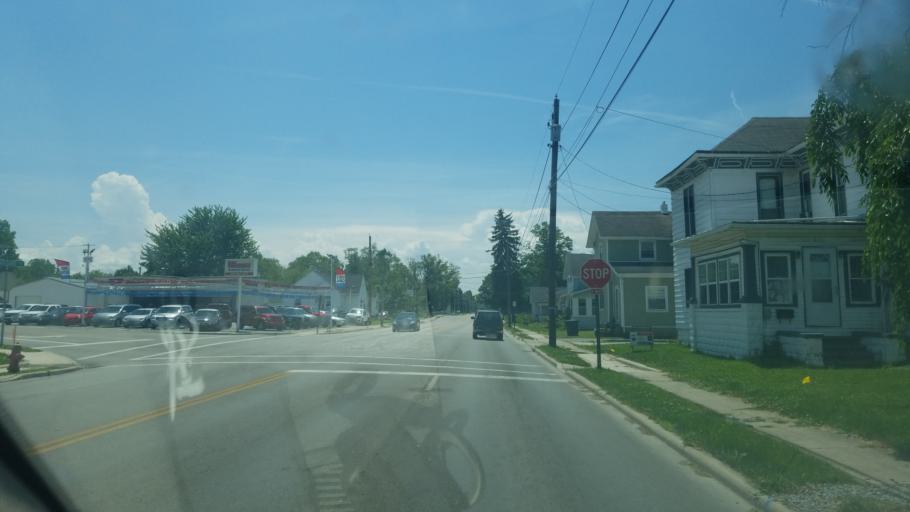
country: US
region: Ohio
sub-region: Hancock County
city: Findlay
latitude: 41.0316
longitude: -83.6412
